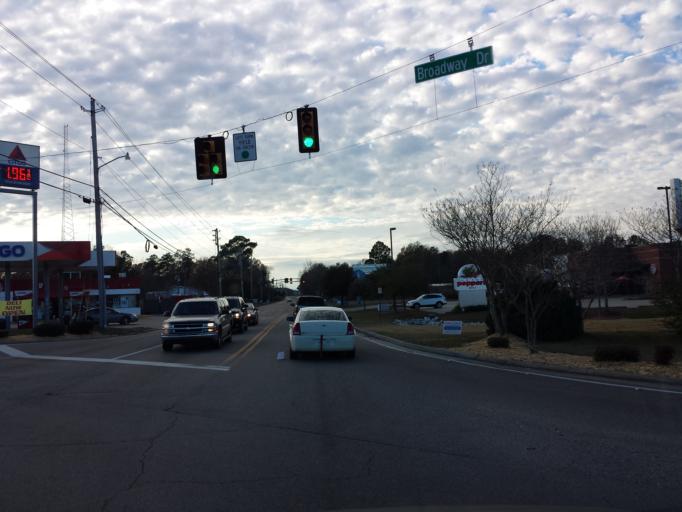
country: US
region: Mississippi
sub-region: Forrest County
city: Hattiesburg
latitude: 31.3041
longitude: -89.3204
